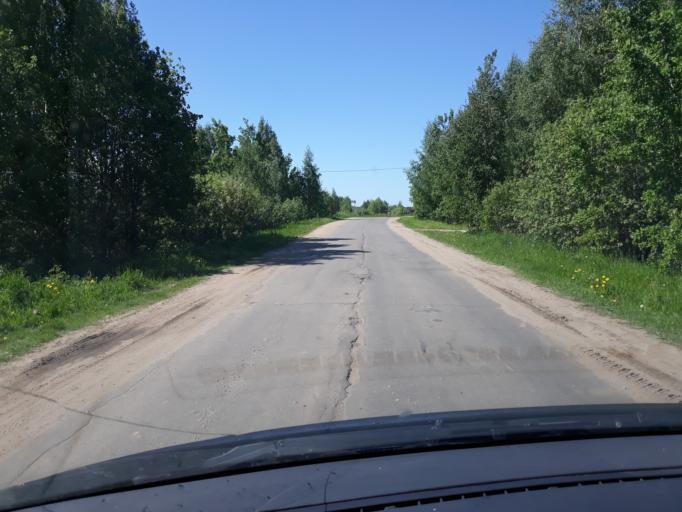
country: RU
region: Jaroslavl
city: Yaroslavl
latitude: 57.6776
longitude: 40.0200
